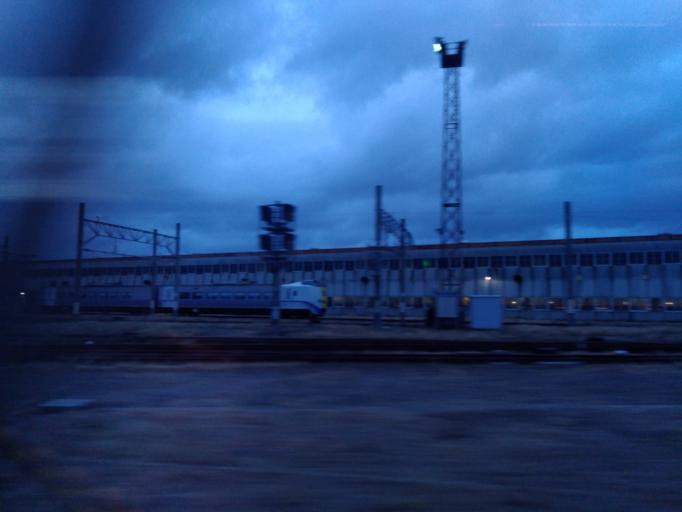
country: JP
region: Hokkaido
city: Hakodate
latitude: 41.7783
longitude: 140.7284
